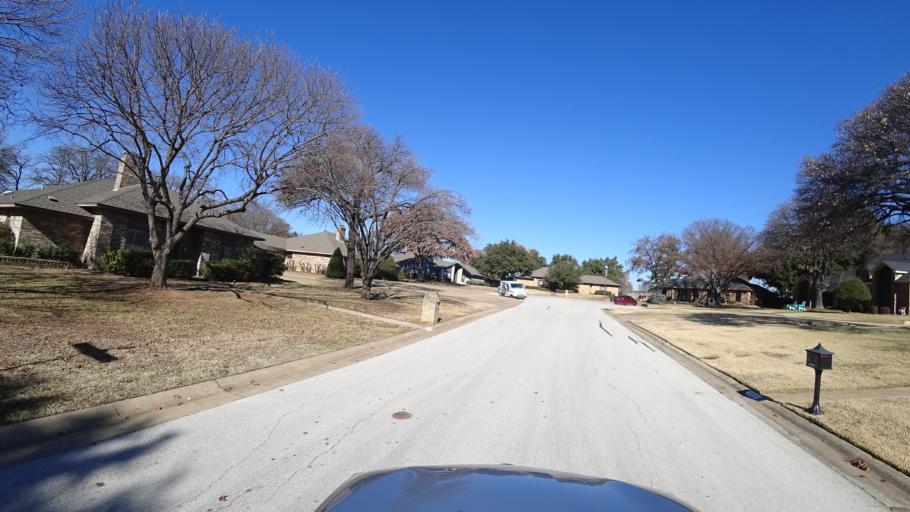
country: US
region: Texas
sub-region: Denton County
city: Lewisville
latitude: 33.0209
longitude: -97.0114
